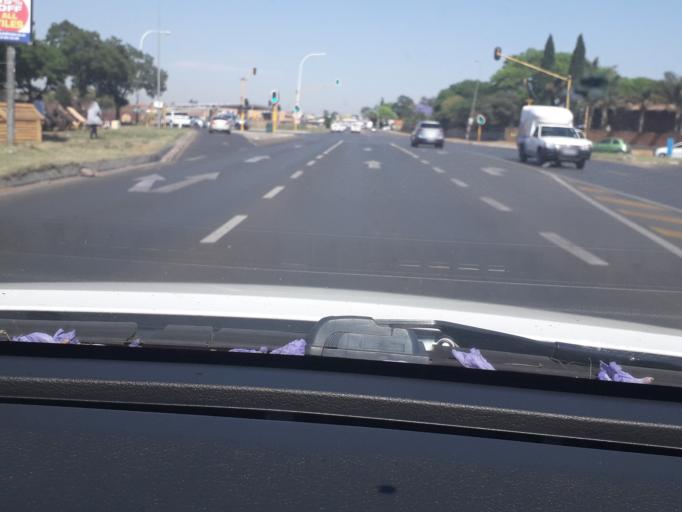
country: ZA
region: Gauteng
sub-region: Ekurhuleni Metropolitan Municipality
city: Boksburg
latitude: -26.1791
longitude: 28.2681
